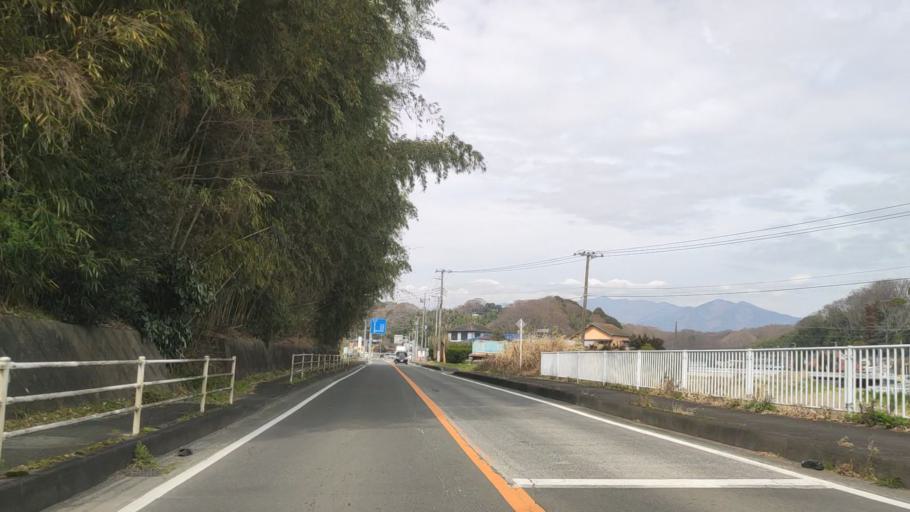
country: JP
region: Kanagawa
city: Hadano
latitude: 35.3288
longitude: 139.2179
